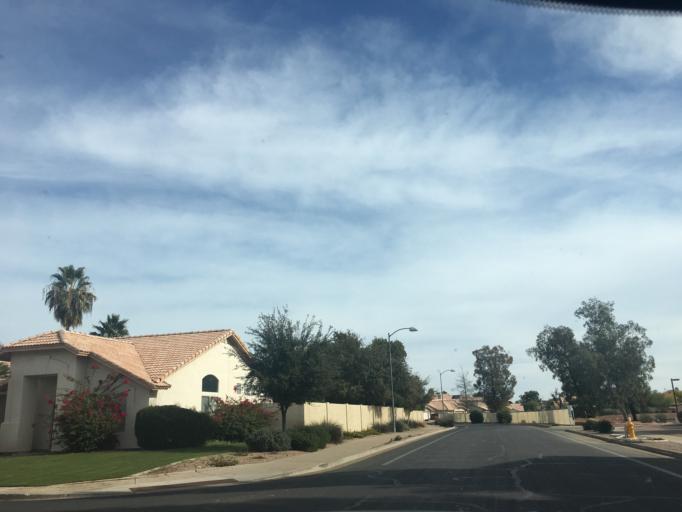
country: US
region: Arizona
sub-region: Maricopa County
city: Gilbert
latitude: 33.3438
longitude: -111.8056
